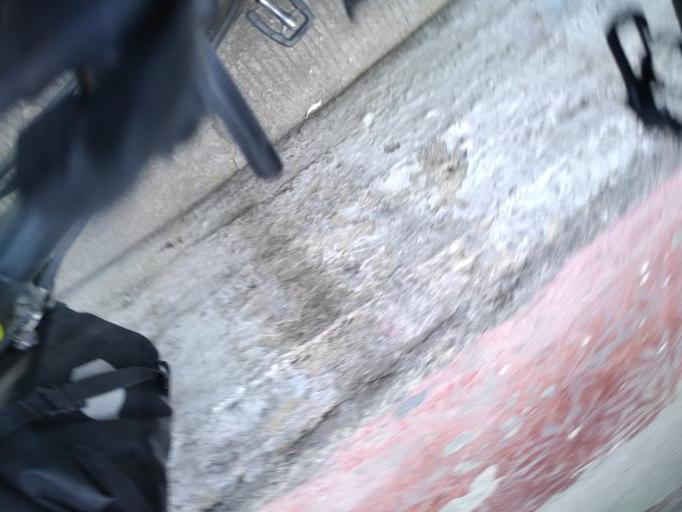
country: EC
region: Zamora-Chinchipe
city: Zamora
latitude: -4.3650
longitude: -79.1772
